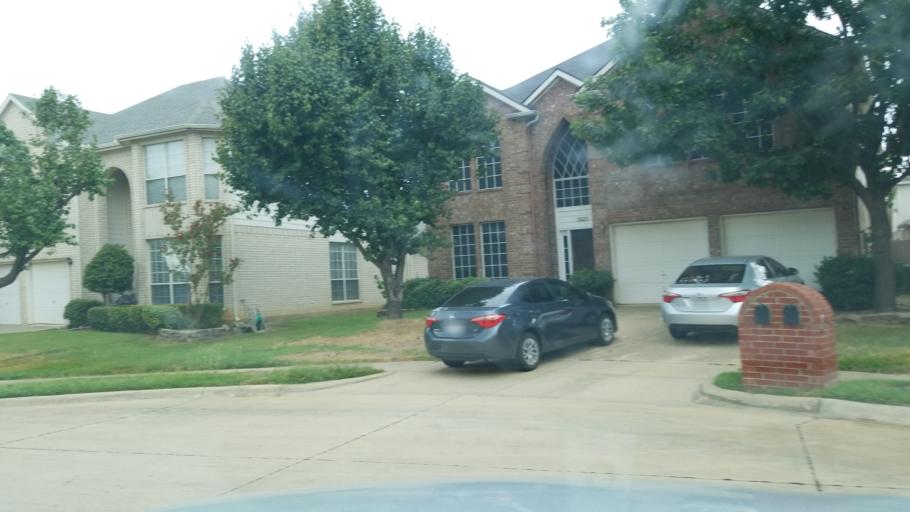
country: US
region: Texas
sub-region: Tarrant County
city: Euless
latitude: 32.8426
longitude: -97.1063
